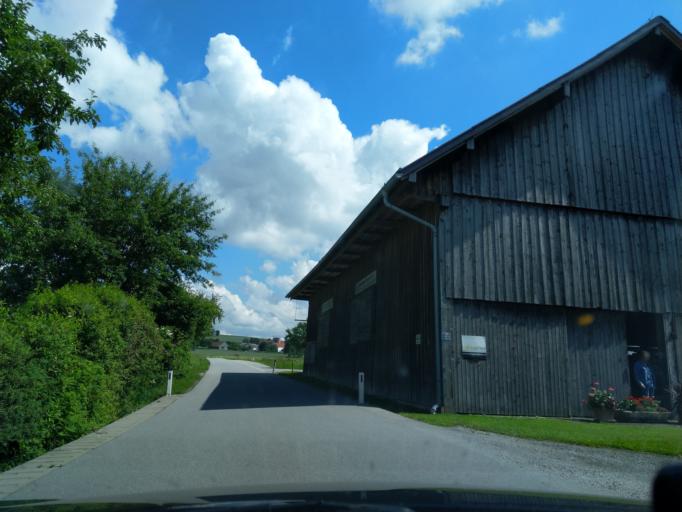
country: DE
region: Bavaria
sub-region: Lower Bavaria
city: Bad Fussing
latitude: 48.3127
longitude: 13.3605
